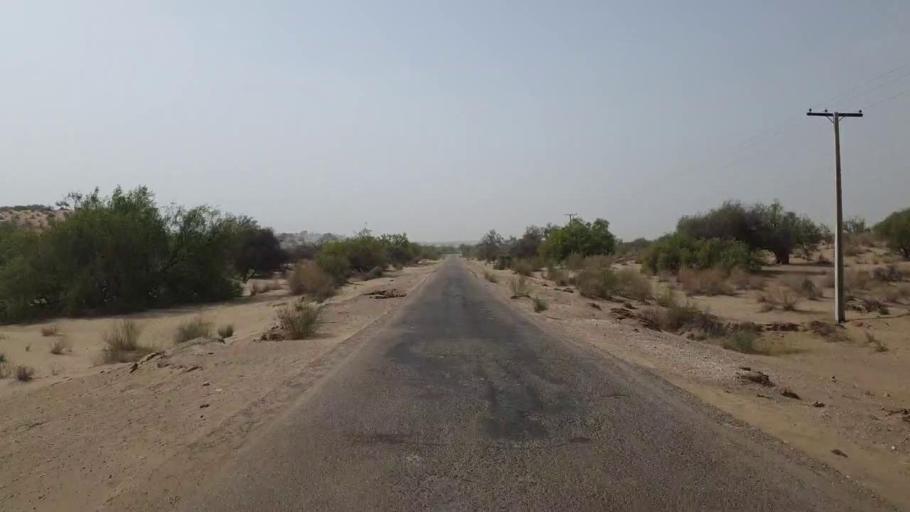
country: PK
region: Sindh
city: Mithi
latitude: 24.6009
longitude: 69.9235
